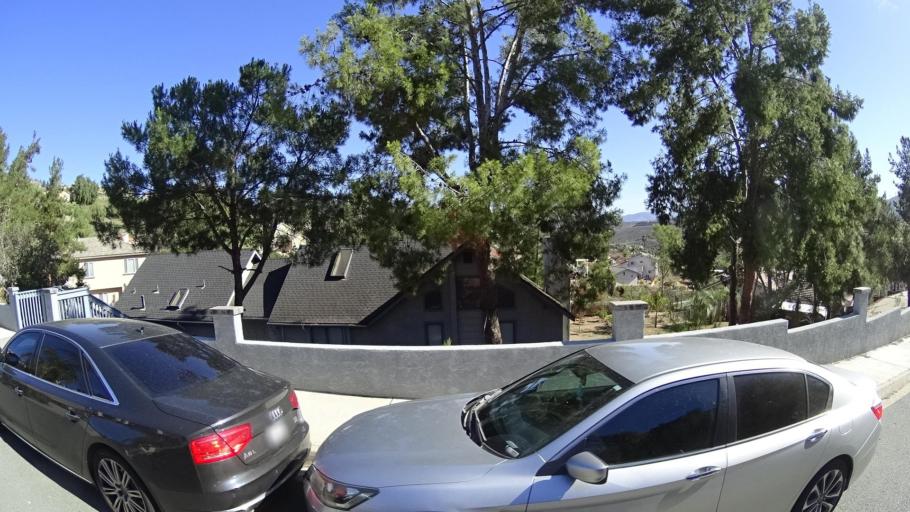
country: US
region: California
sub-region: San Diego County
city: La Presa
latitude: 32.7183
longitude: -116.9828
